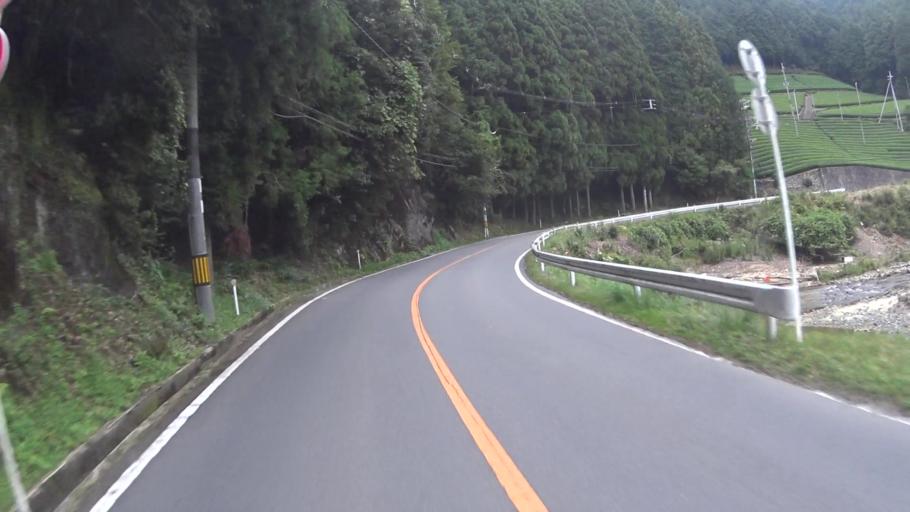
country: JP
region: Kyoto
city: Uji
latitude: 34.8217
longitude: 135.9286
